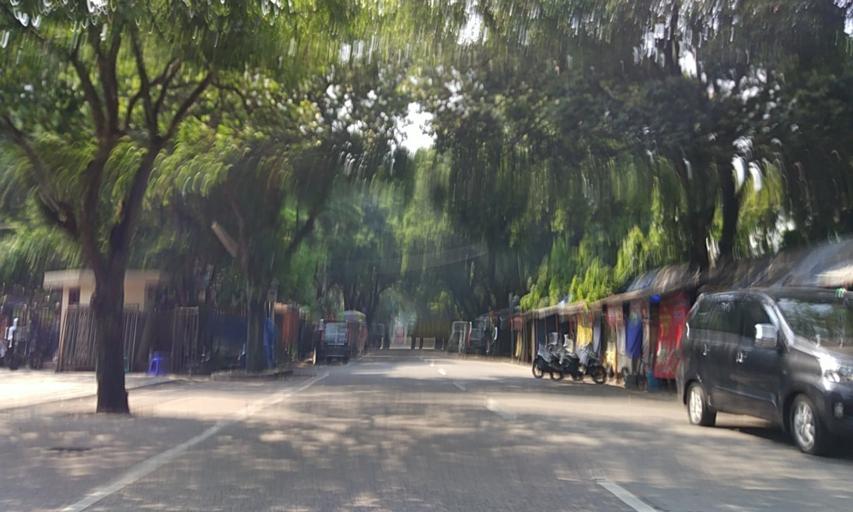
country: ID
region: West Java
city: Bandung
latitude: -6.9039
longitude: 107.5989
